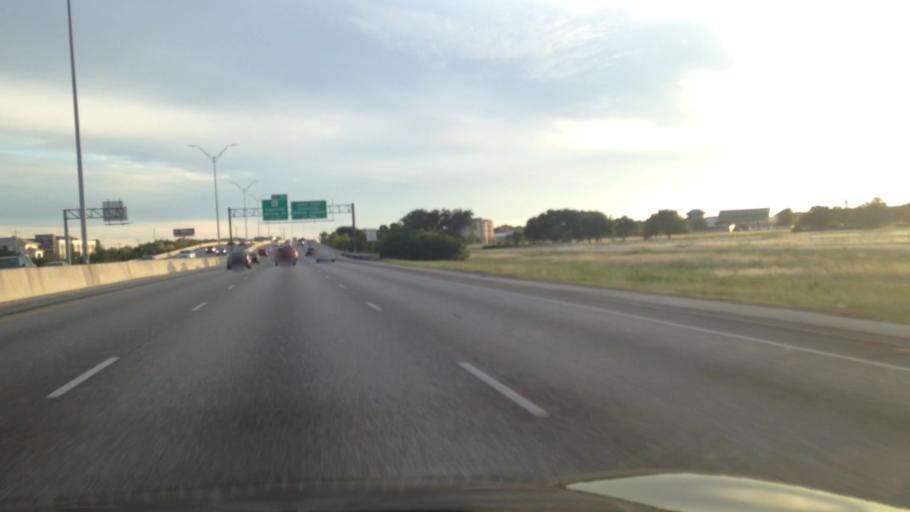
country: US
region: Texas
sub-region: Hays County
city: San Marcos
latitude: 29.9090
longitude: -97.9000
